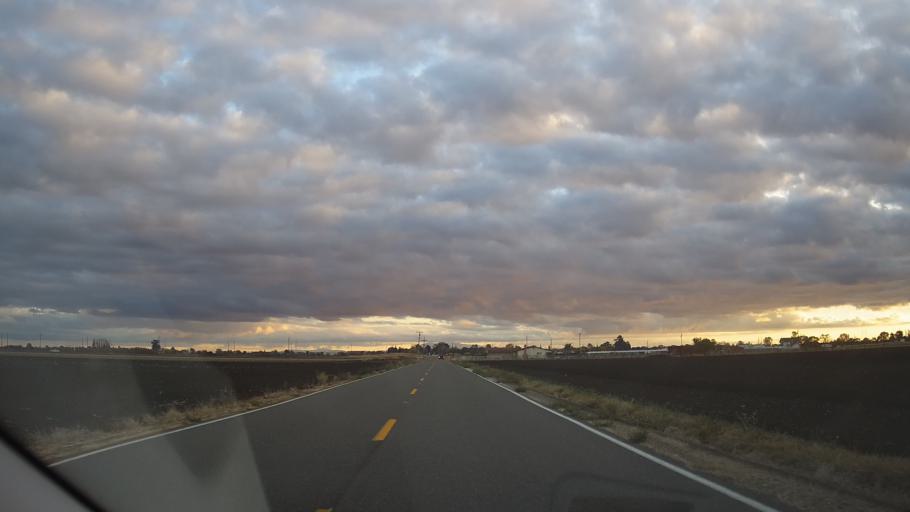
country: US
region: California
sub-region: Solano County
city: Hartley
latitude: 38.3631
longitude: -121.9060
